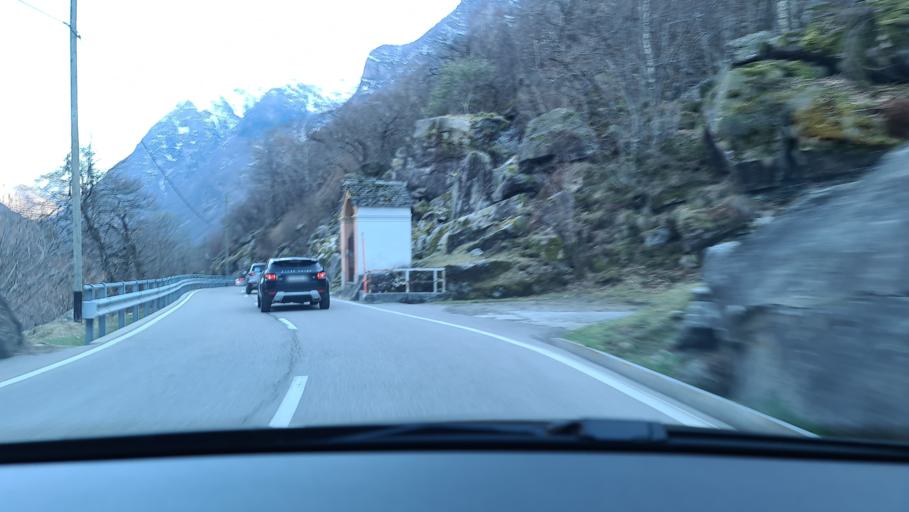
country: CH
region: Ticino
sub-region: Locarno District
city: Lavertezzo
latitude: 46.2885
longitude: 8.7960
